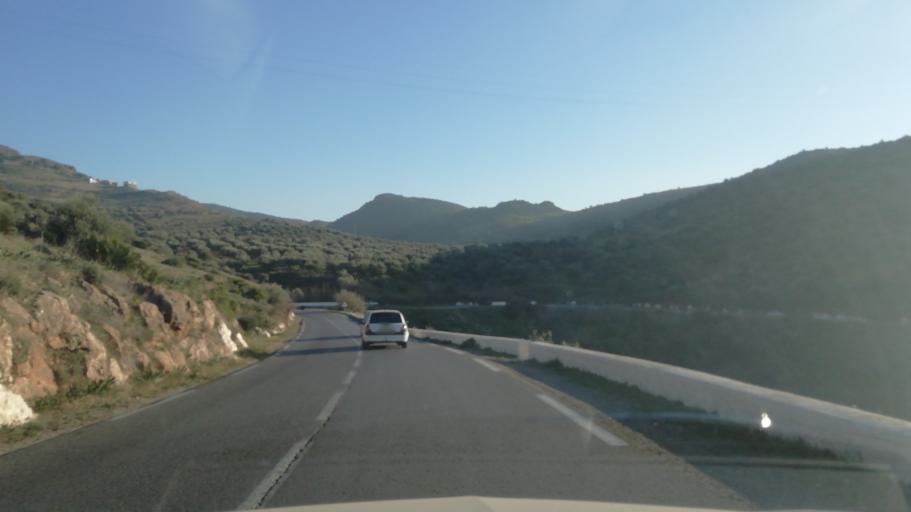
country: DZ
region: Tlemcen
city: Beni Mester
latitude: 34.8509
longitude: -1.4511
